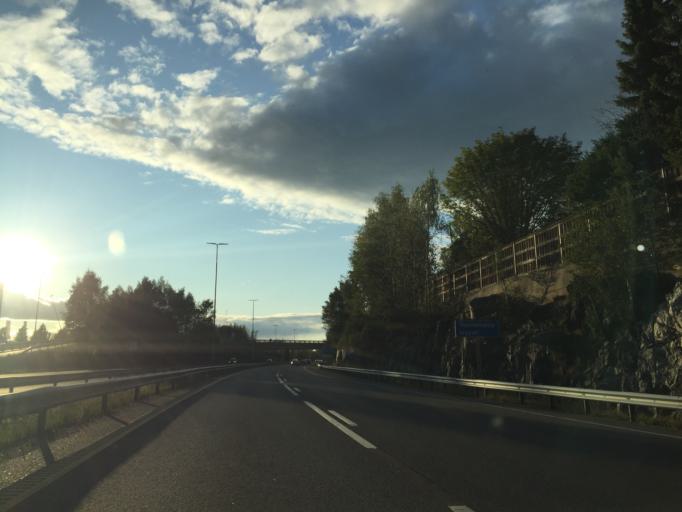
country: NO
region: Akershus
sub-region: Lorenskog
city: Kjenn
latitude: 59.9295
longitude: 10.9503
